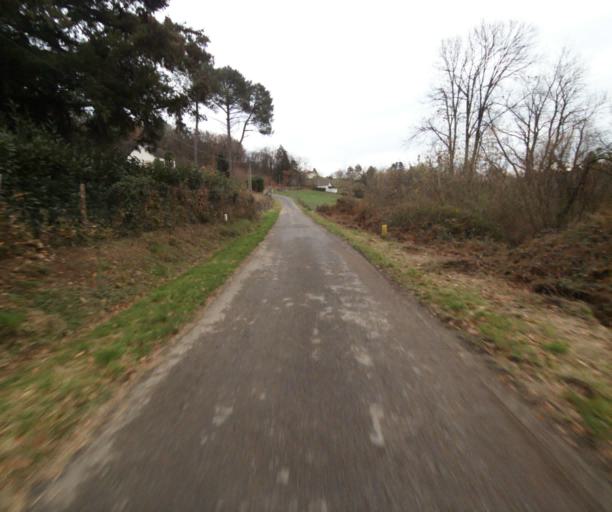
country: FR
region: Limousin
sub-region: Departement de la Correze
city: Cornil
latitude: 45.2317
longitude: 1.6536
